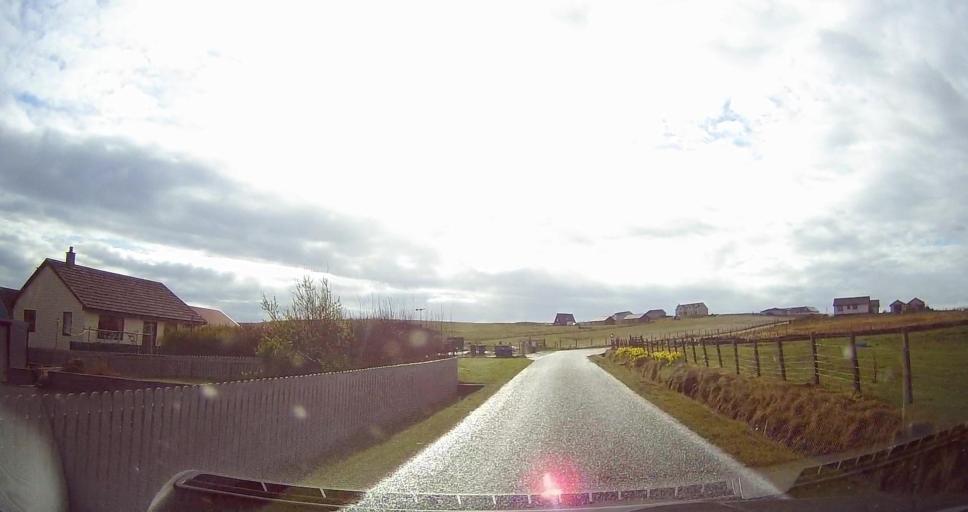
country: GB
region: Scotland
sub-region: Shetland Islands
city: Sandwick
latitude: 60.0602
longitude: -1.2174
